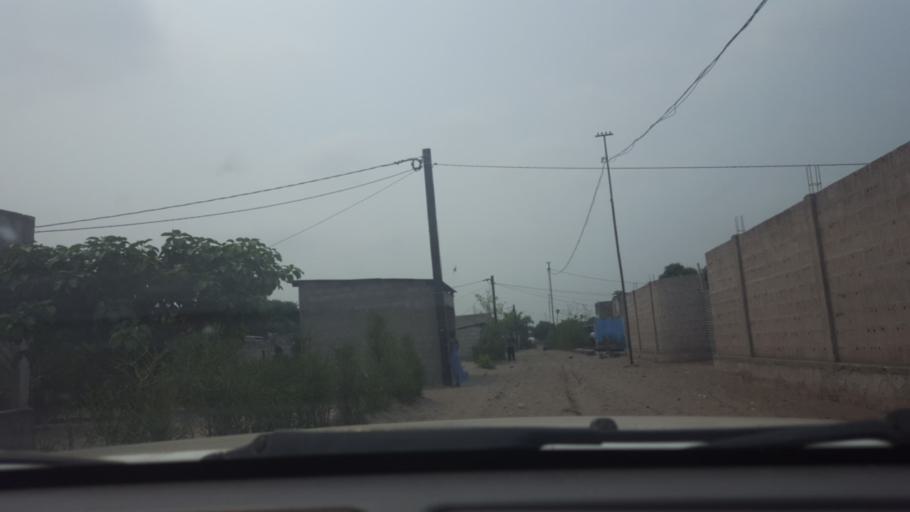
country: CD
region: Kinshasa
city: Masina
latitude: -4.3561
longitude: 15.5094
